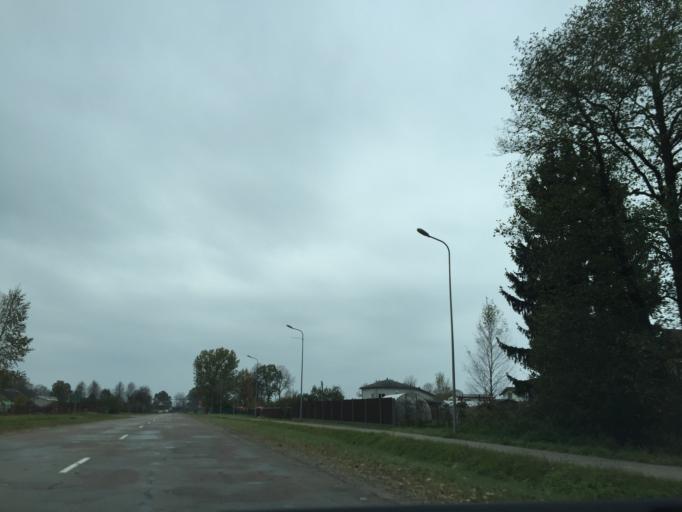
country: LV
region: Marupe
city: Marupe
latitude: 56.8479
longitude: 24.0490
